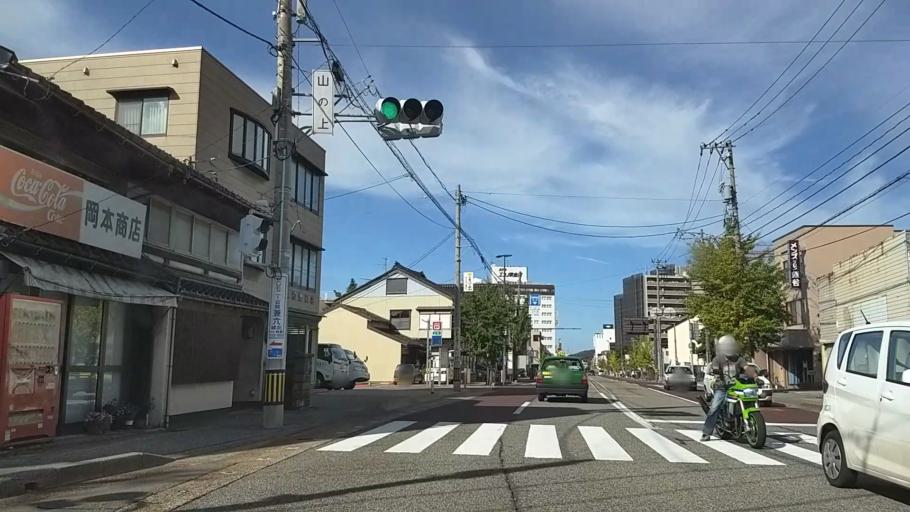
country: JP
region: Ishikawa
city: Kanazawa-shi
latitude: 36.5797
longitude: 136.6702
